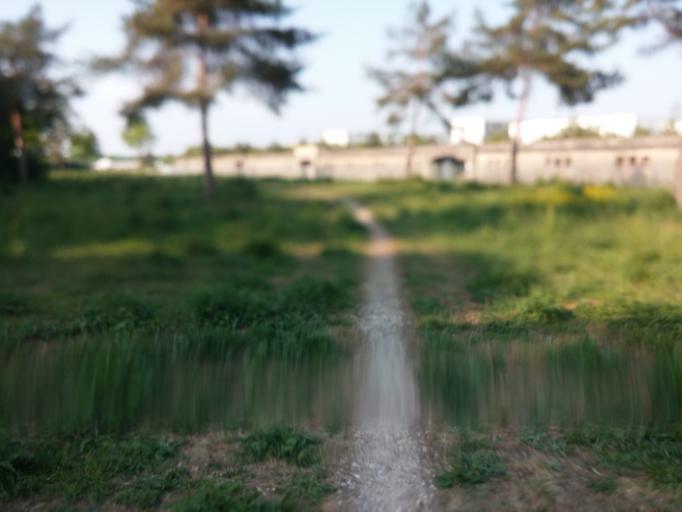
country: DE
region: Bavaria
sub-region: Upper Bavaria
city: Haar
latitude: 48.1314
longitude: 11.6823
